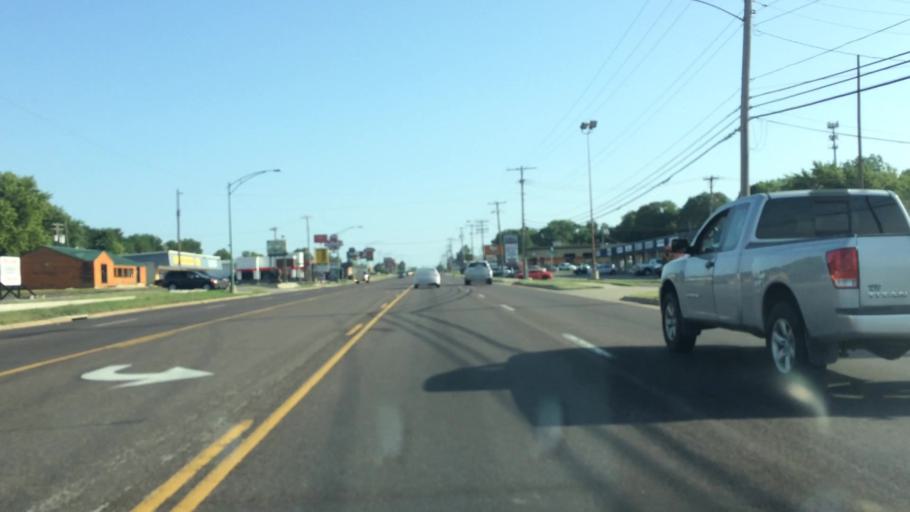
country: US
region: Missouri
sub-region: Greene County
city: Springfield
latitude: 37.1725
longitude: -93.2953
